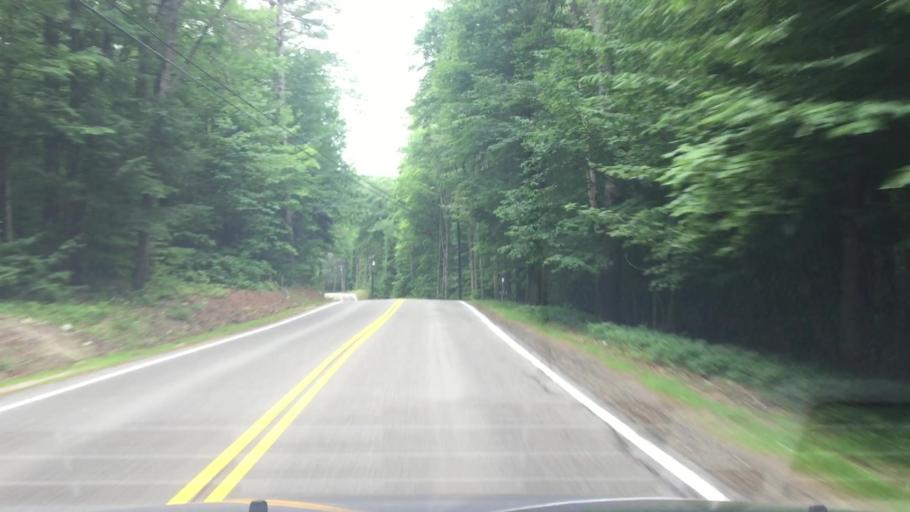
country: US
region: New Hampshire
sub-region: Carroll County
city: Madison
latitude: 43.8997
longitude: -71.0730
